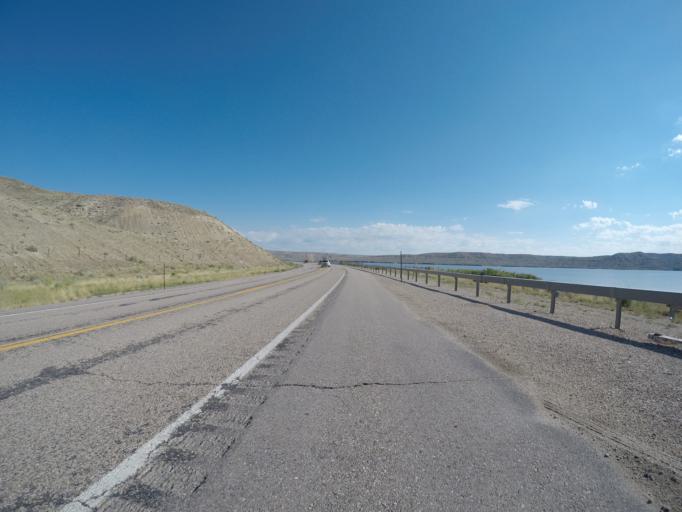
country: US
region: Wyoming
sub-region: Sublette County
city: Marbleton
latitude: 42.1060
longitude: -110.1395
